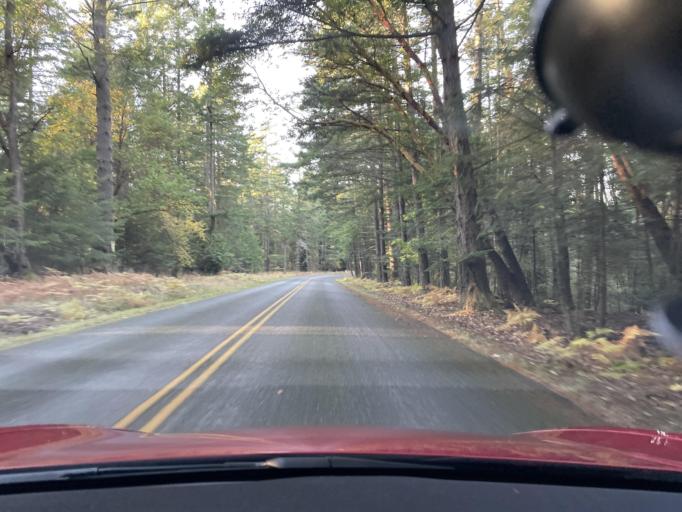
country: US
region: Washington
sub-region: San Juan County
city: Friday Harbor
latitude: 48.5330
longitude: -123.1587
